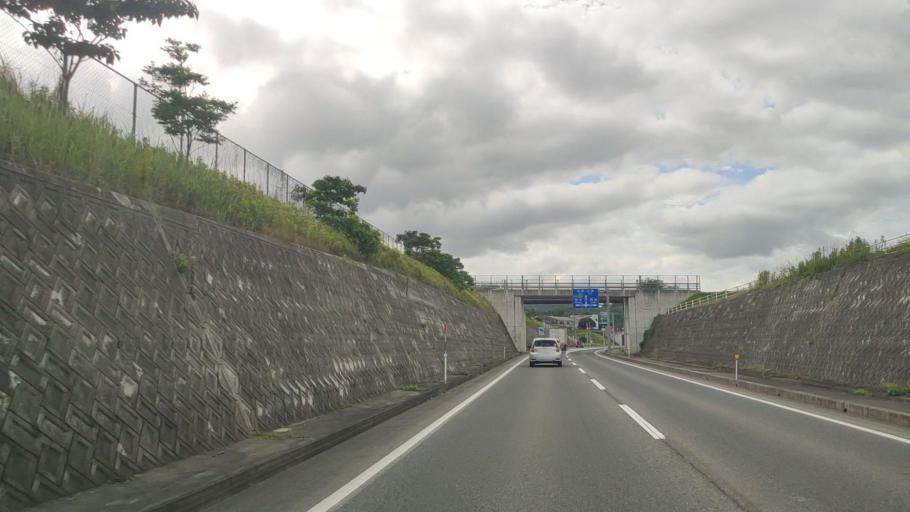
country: JP
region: Tottori
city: Yonago
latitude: 35.3850
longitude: 133.3858
